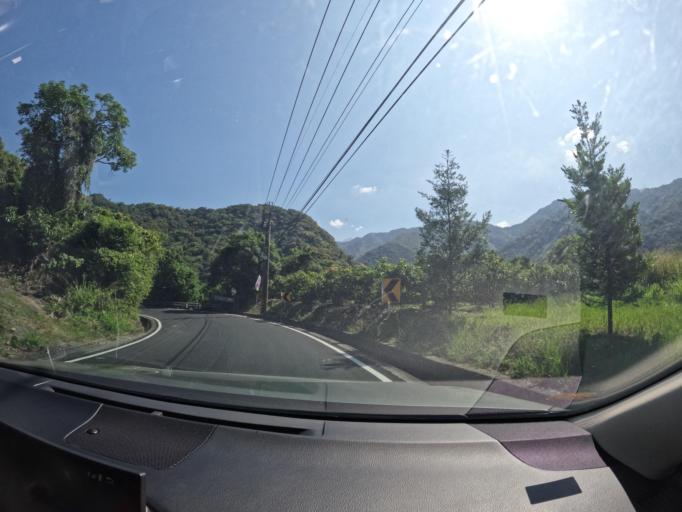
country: TW
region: Taiwan
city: Yujing
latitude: 23.1356
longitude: 120.7270
